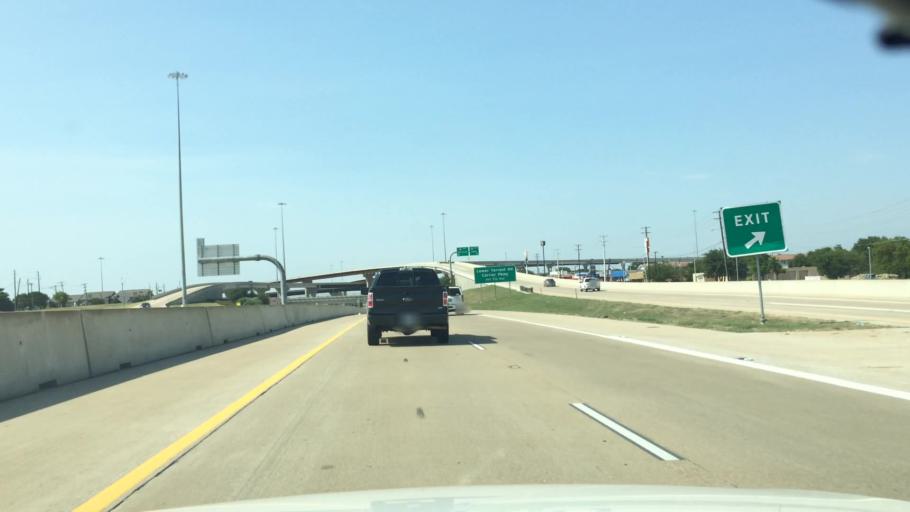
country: US
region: Texas
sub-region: Dallas County
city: Grand Prairie
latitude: 32.7538
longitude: -97.0290
